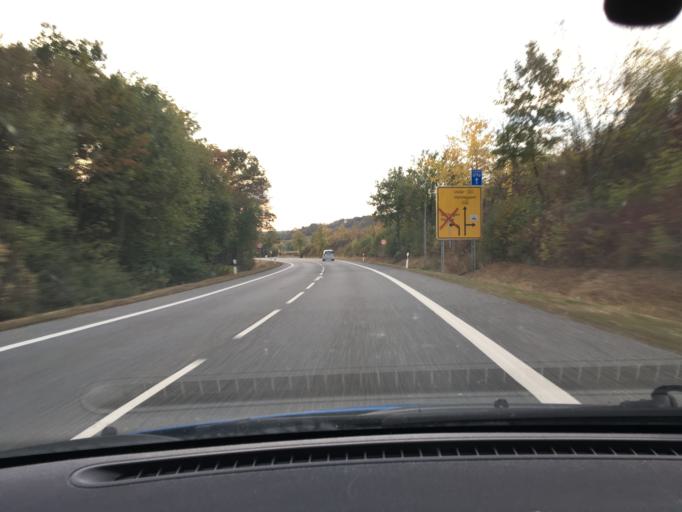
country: DE
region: Lower Saxony
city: Hardegsen
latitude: 51.6441
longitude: 9.8632
